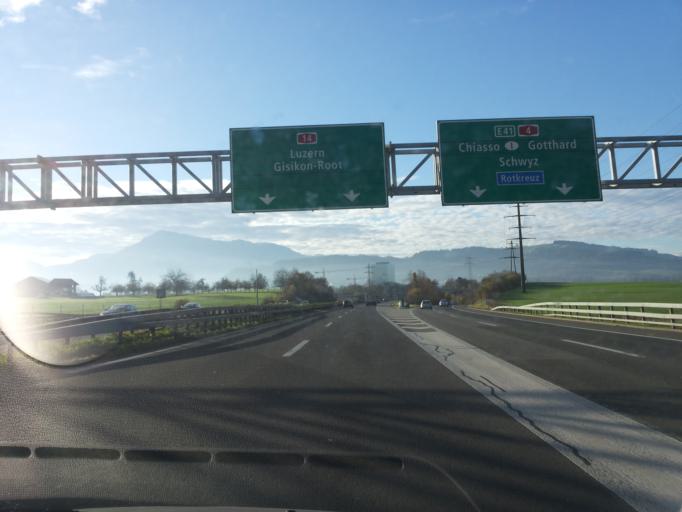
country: CH
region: Zug
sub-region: Zug
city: Hunenberg
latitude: 47.1609
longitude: 8.4329
